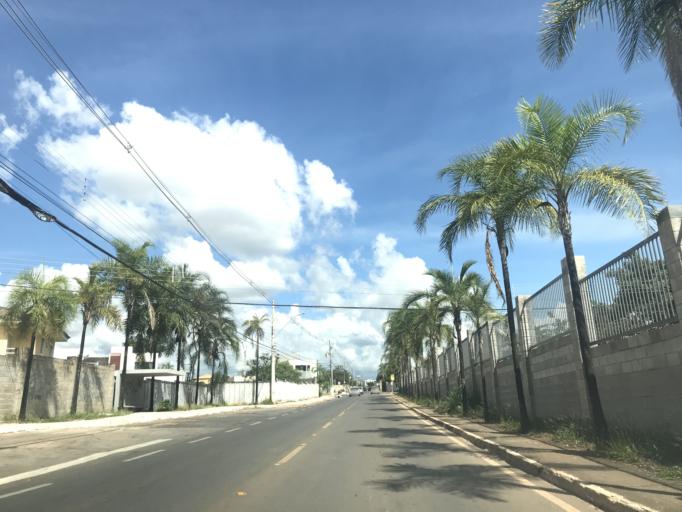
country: BR
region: Federal District
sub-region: Brasilia
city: Brasilia
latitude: -15.8687
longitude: -47.7962
